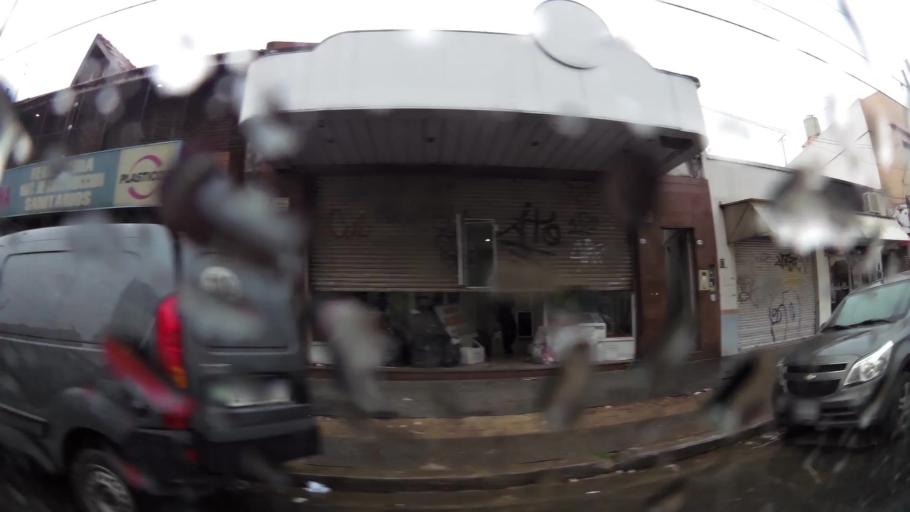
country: AR
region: Buenos Aires
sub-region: Partido de Lanus
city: Lanus
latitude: -34.7058
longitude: -58.4169
